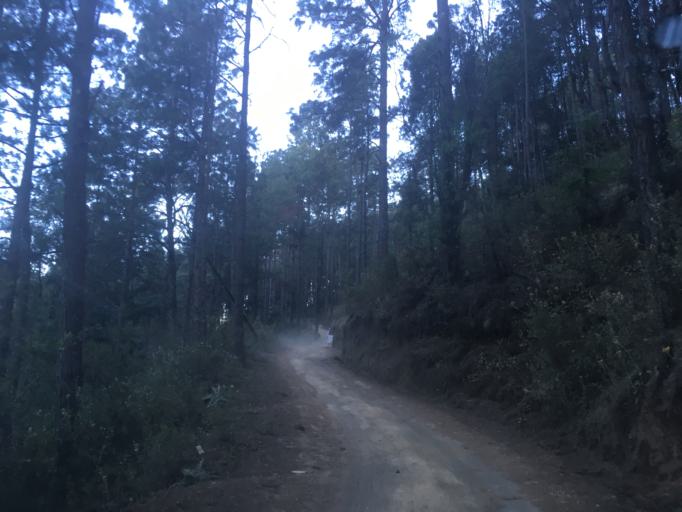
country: MX
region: Michoacan
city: Angahuan
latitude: 19.4727
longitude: -102.2410
